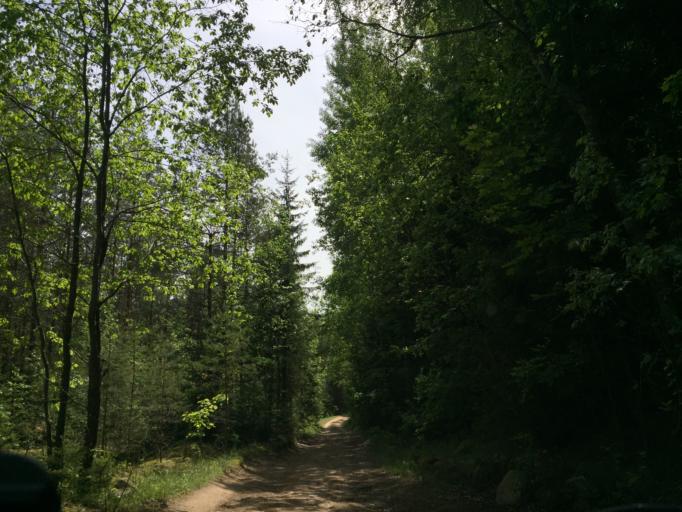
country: LV
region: Koceni
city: Koceni
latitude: 57.4423
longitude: 25.2829
